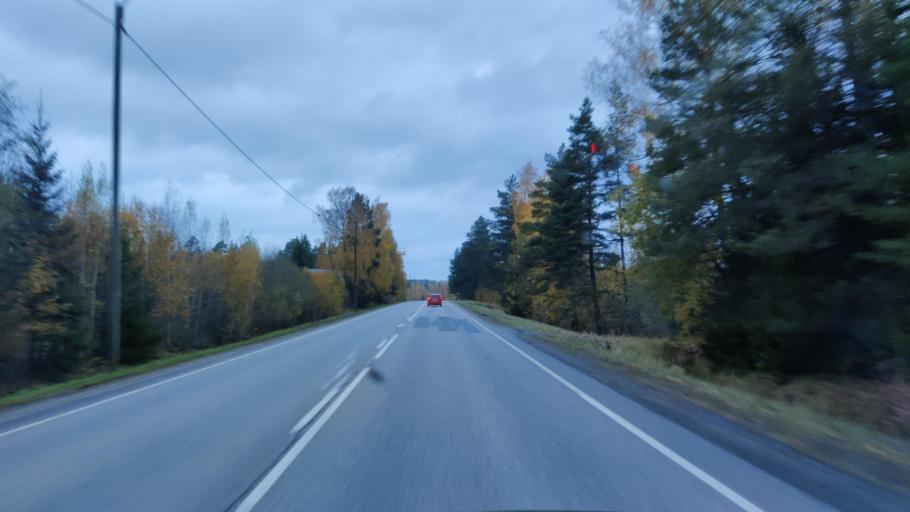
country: FI
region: Uusimaa
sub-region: Helsinki
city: Vihti
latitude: 60.3495
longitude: 24.1884
